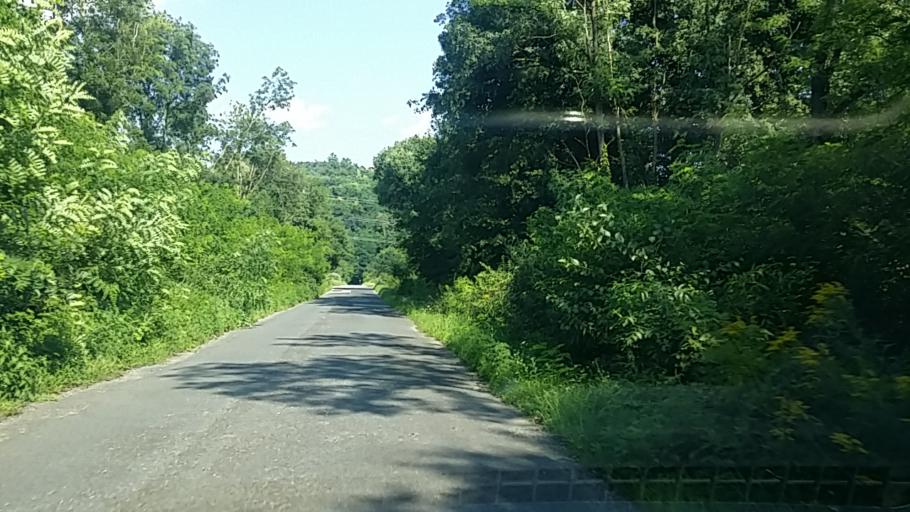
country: HU
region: Zala
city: Lenti
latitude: 46.5540
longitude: 16.5871
